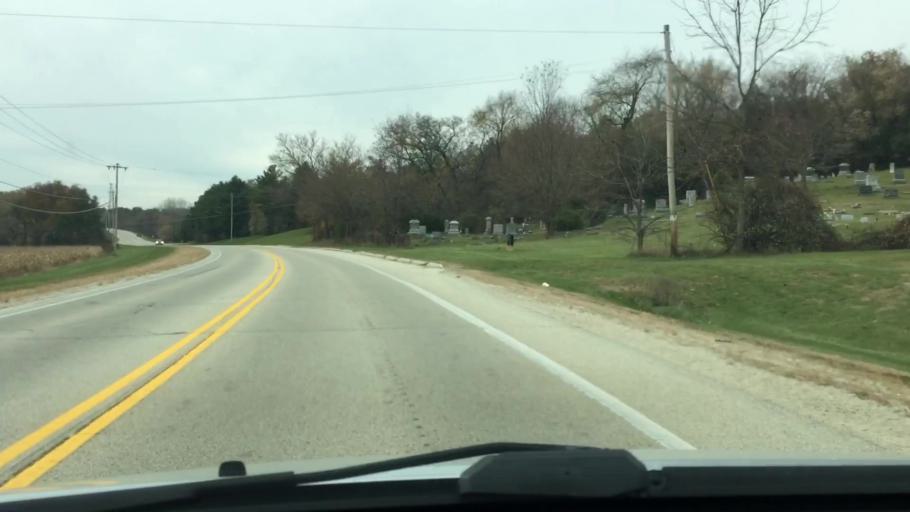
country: US
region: Wisconsin
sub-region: Waukesha County
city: Big Bend
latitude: 42.9025
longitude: -88.2604
